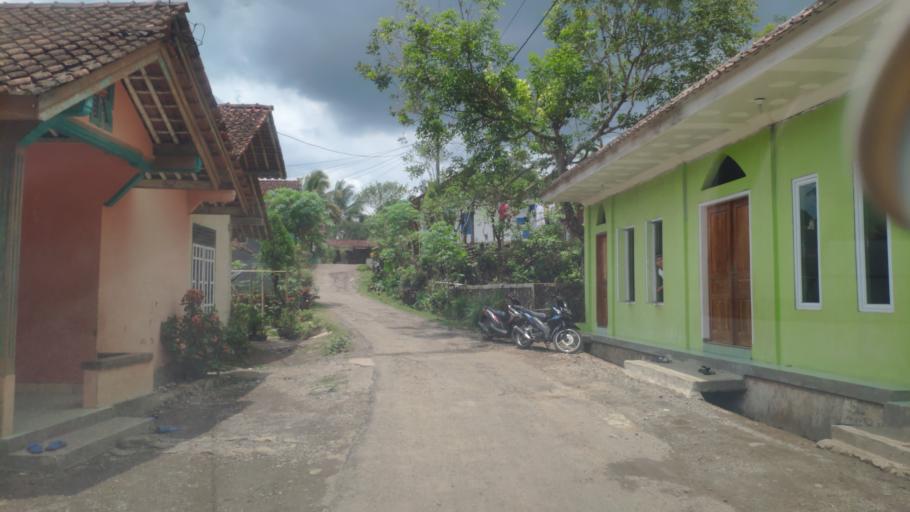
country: ID
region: Central Java
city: Purbalingga
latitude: -7.3140
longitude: 109.5894
